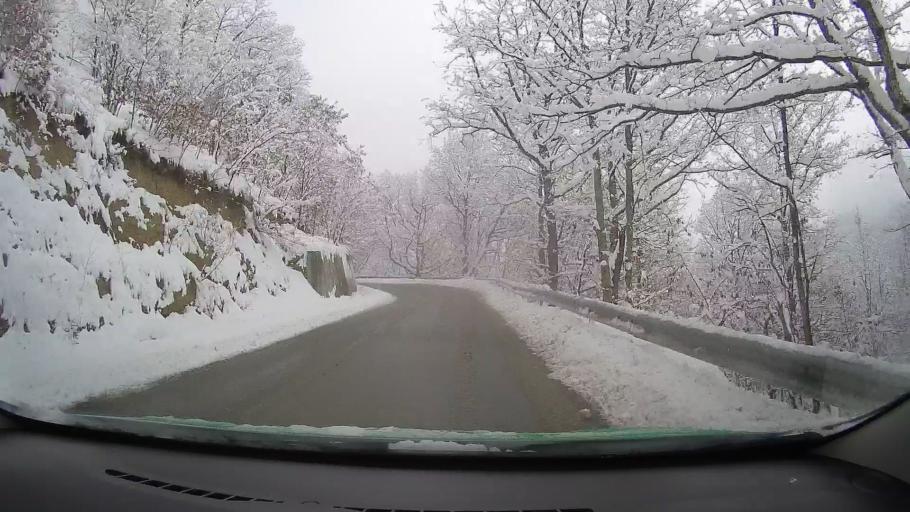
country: RO
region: Alba
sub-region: Comuna Sugag
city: Dobra
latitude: 45.7609
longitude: 23.6665
